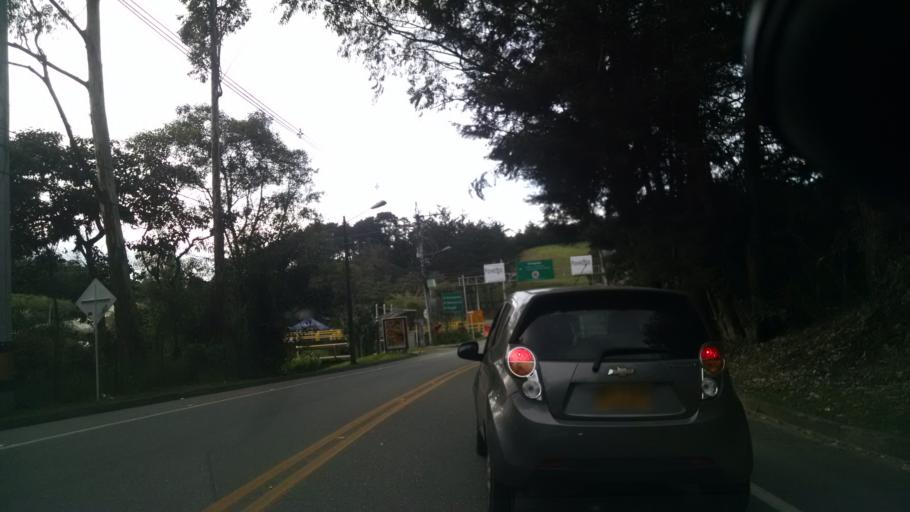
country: CO
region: Antioquia
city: Envigado
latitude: 6.1428
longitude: -75.5238
